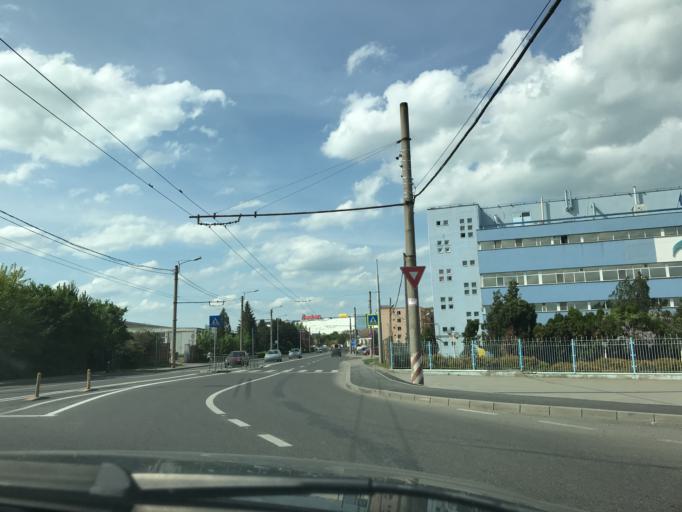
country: RO
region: Cluj
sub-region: Municipiul Cluj-Napoca
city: Cluj-Napoca
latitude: 46.7953
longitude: 23.6140
